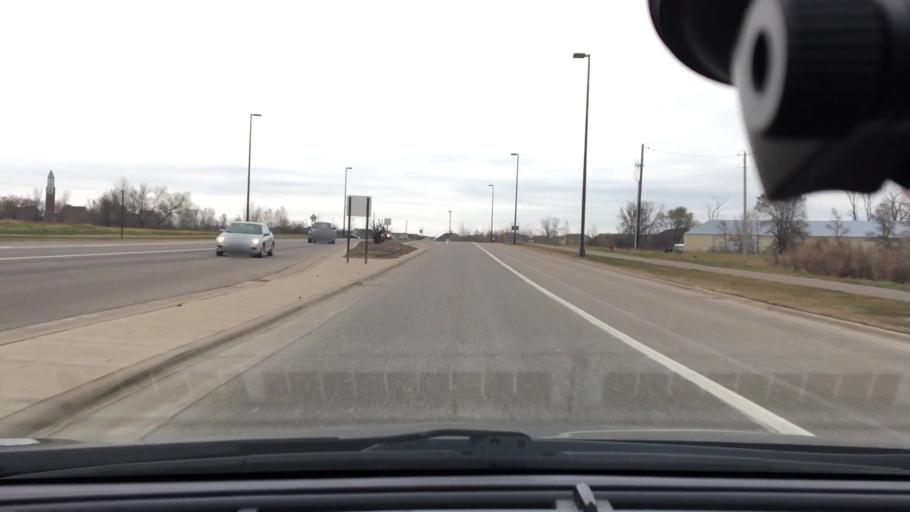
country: US
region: Minnesota
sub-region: Hennepin County
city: Corcoran
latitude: 45.0865
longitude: -93.5162
